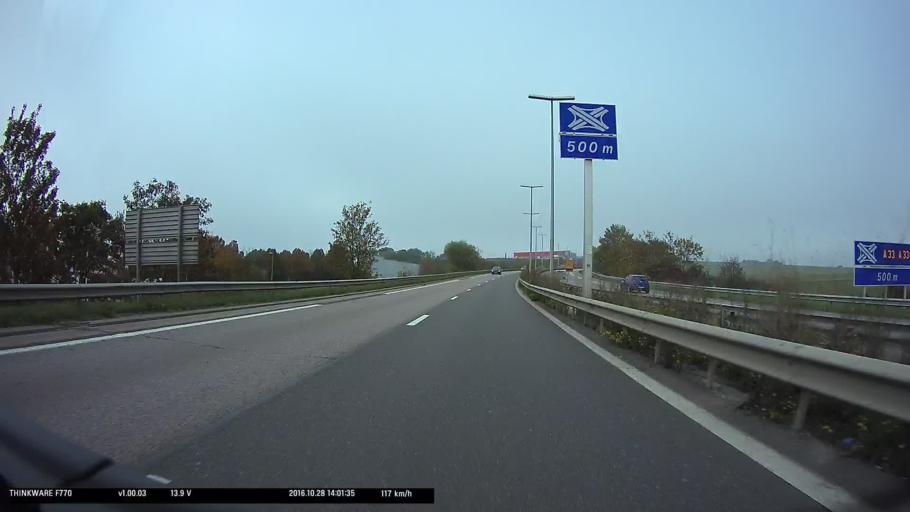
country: FR
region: Lorraine
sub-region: Departement de Meurthe-et-Moselle
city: Fleville-devant-Nancy
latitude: 48.6188
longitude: 6.1940
